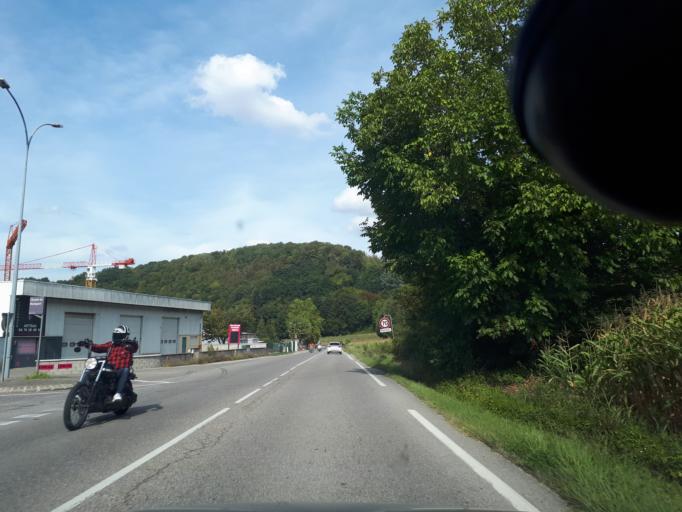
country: FR
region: Rhone-Alpes
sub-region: Departement de l'Isere
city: Maubec
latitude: 45.5653
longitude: 5.2787
